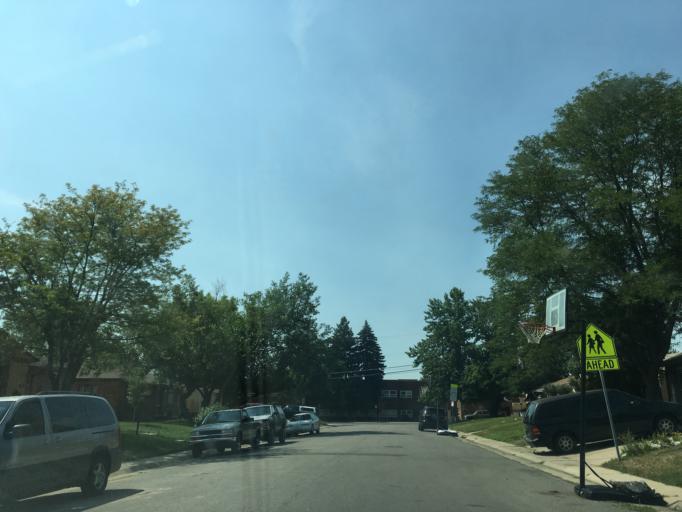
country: US
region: Colorado
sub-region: Jefferson County
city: Lakewood
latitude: 39.6904
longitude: -105.0471
